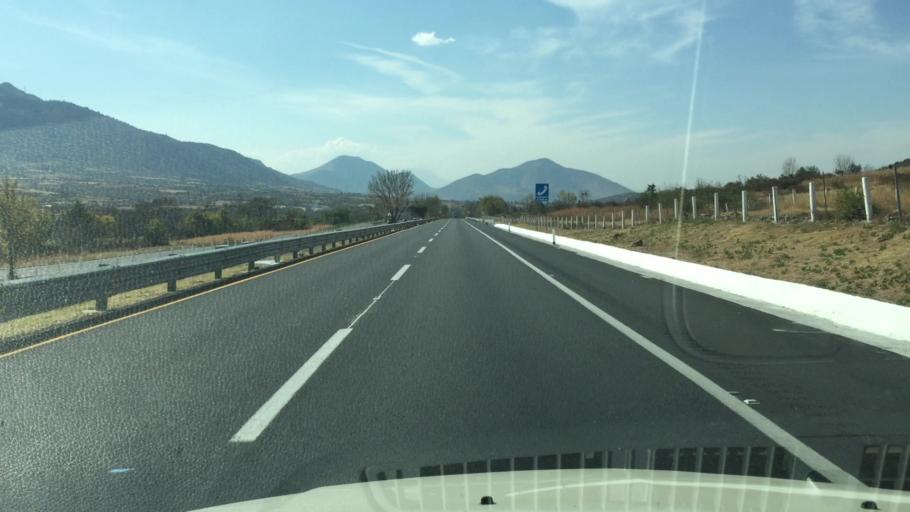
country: MX
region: Michoacan
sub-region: Contepec
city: Atotonilco
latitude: 19.8776
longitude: -100.2268
